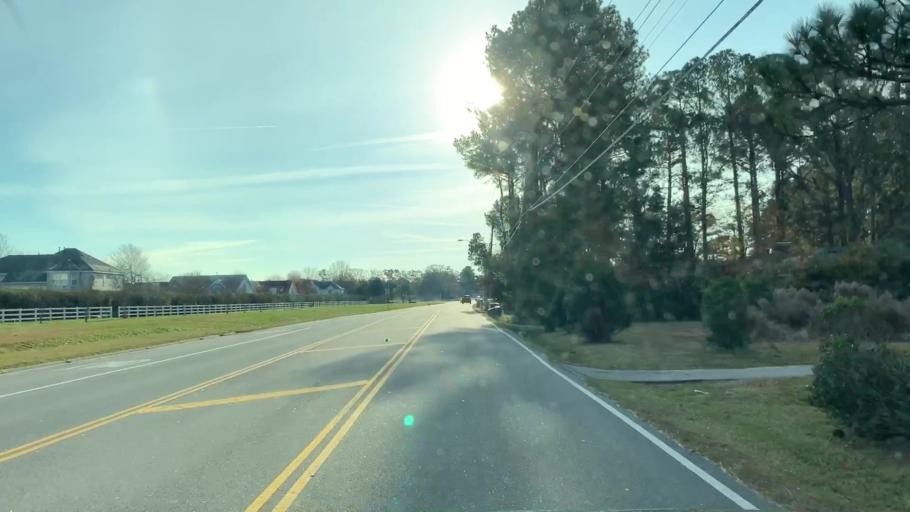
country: US
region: Virginia
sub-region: City of Chesapeake
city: Chesapeake
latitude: 36.7597
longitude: -76.1380
